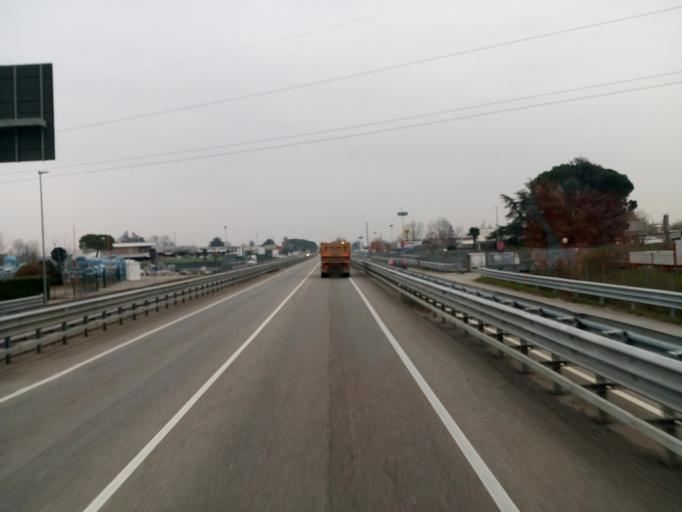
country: IT
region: Friuli Venezia Giulia
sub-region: Provincia di Udine
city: Pradamano
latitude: 46.0207
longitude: 13.2754
